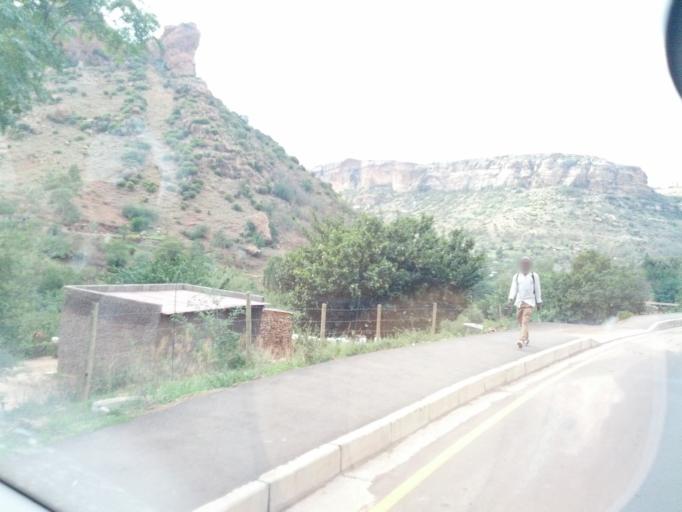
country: LS
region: Maseru
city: Nako
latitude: -29.4728
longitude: 27.7393
